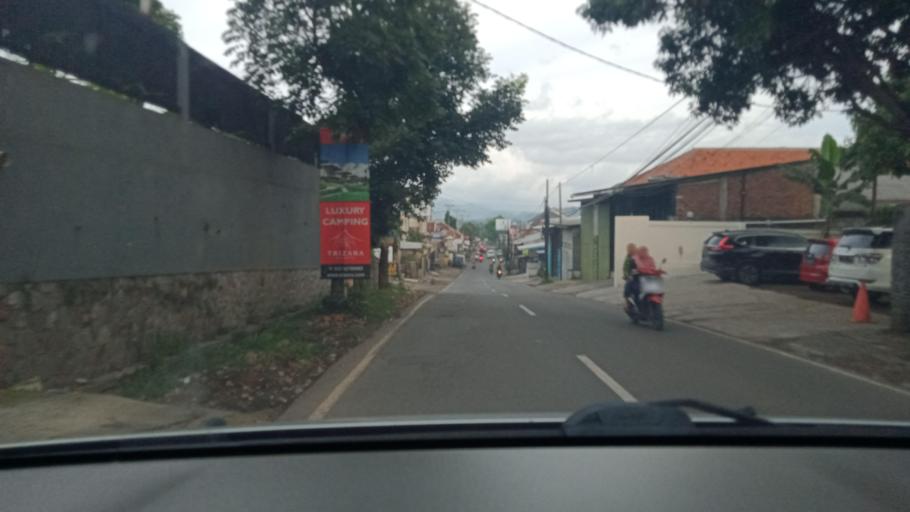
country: ID
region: West Java
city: Lembang
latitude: -6.8046
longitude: 107.5918
